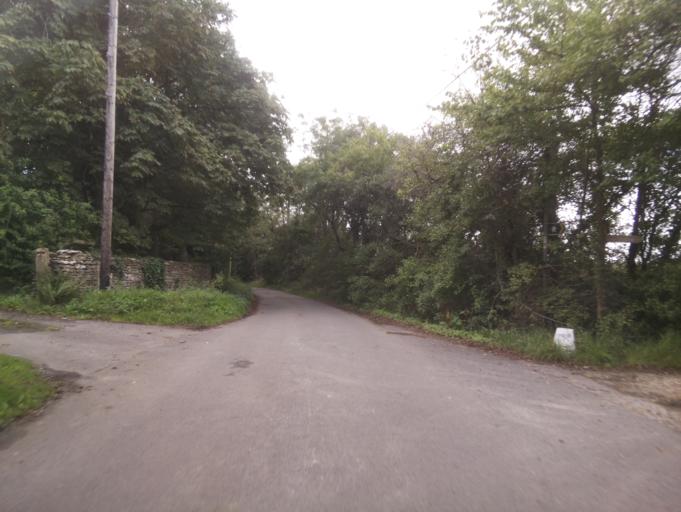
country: GB
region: England
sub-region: Wiltshire
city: Nettleton
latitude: 51.5034
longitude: -2.2642
